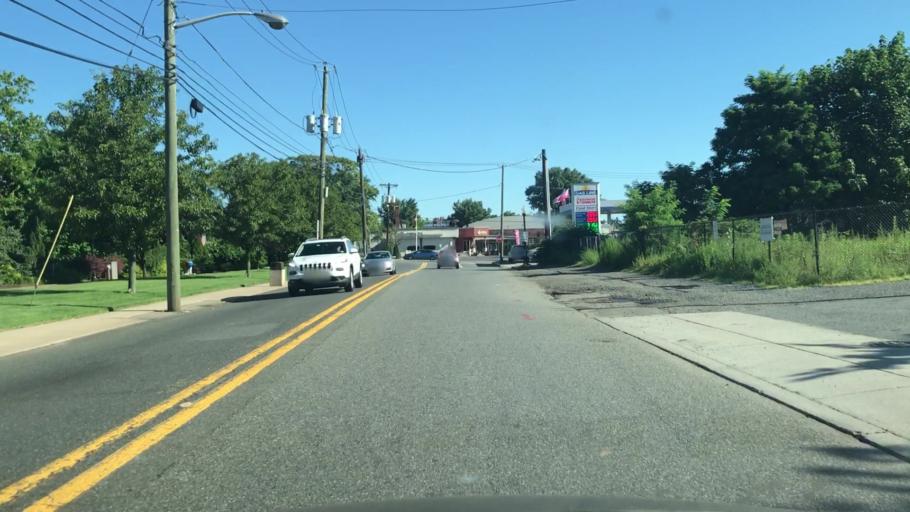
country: US
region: New Jersey
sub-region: Bergen County
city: Wallington
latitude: 40.8535
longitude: -74.1187
